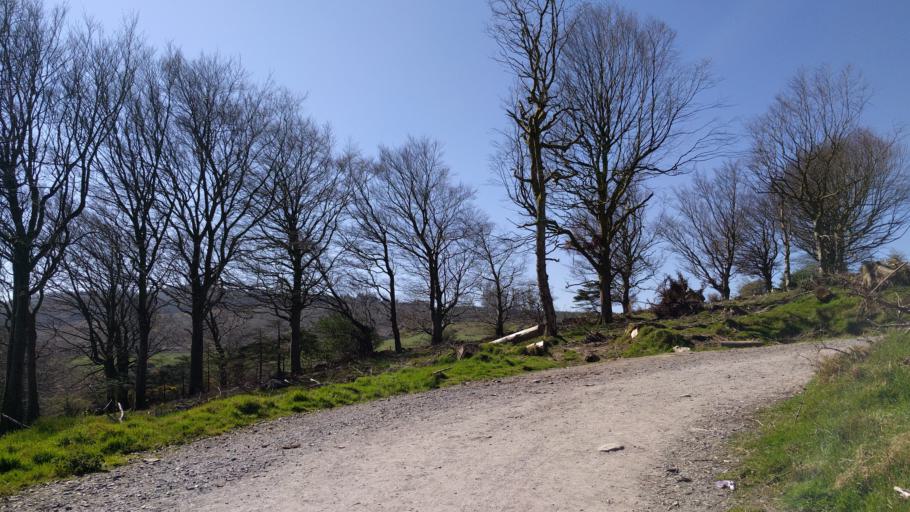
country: IE
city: Knocklyon
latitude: 53.2502
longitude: -6.3233
